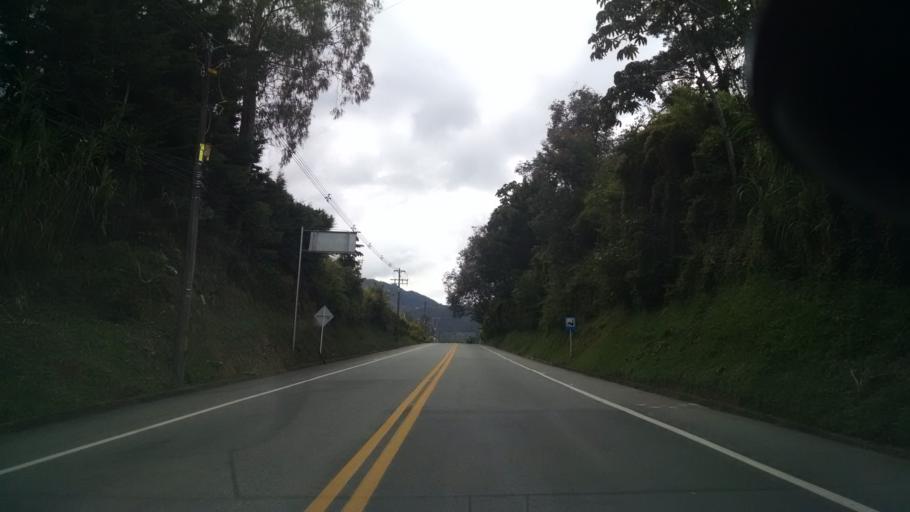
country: CO
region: Antioquia
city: El Retiro
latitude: 6.0934
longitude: -75.4962
